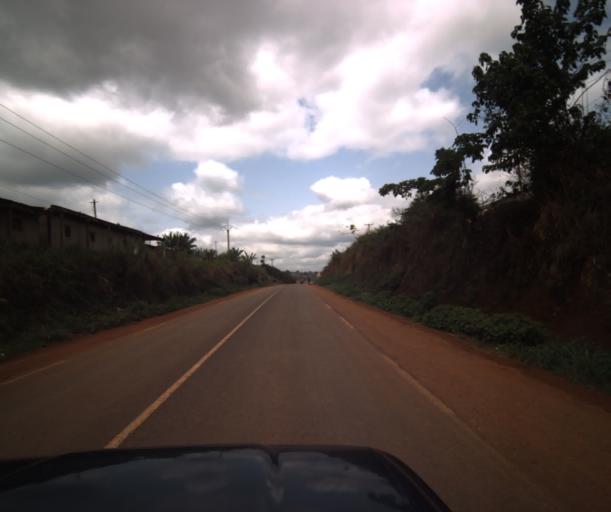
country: CM
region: Centre
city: Yaounde
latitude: 3.7944
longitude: 11.4891
